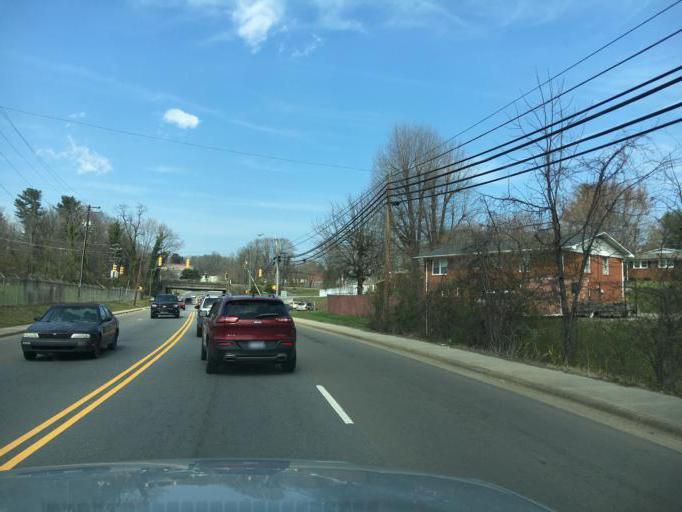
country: US
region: North Carolina
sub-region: McDowell County
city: Marion
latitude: 35.6787
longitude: -82.0115
